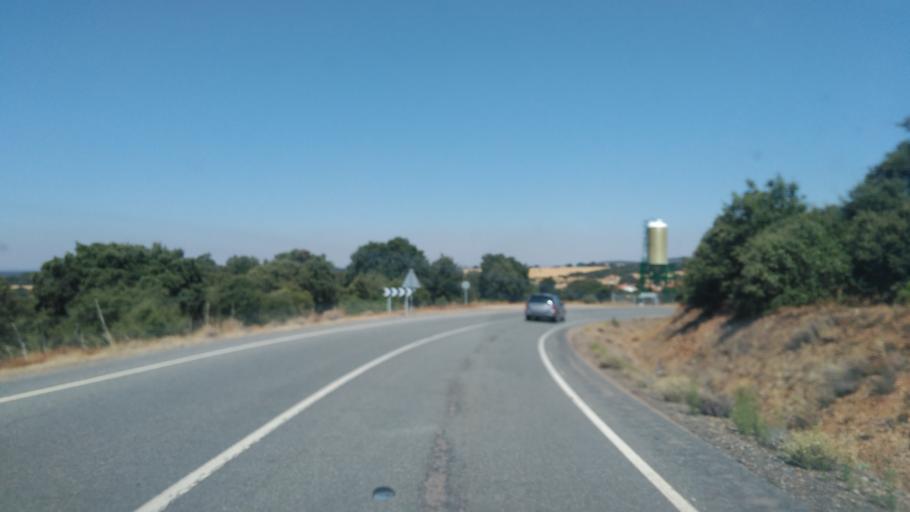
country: ES
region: Castille and Leon
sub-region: Provincia de Salamanca
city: Aldeanueva de la Sierra
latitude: 40.6111
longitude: -6.0974
